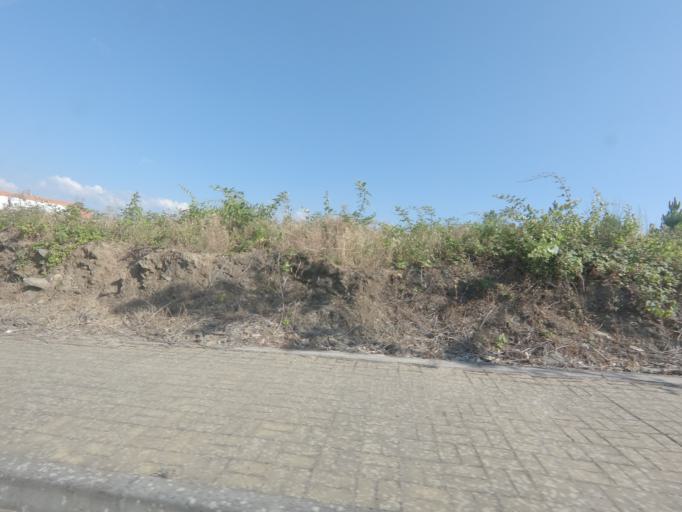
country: PT
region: Vila Real
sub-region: Sabrosa
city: Sabrosa
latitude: 41.2627
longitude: -7.5787
